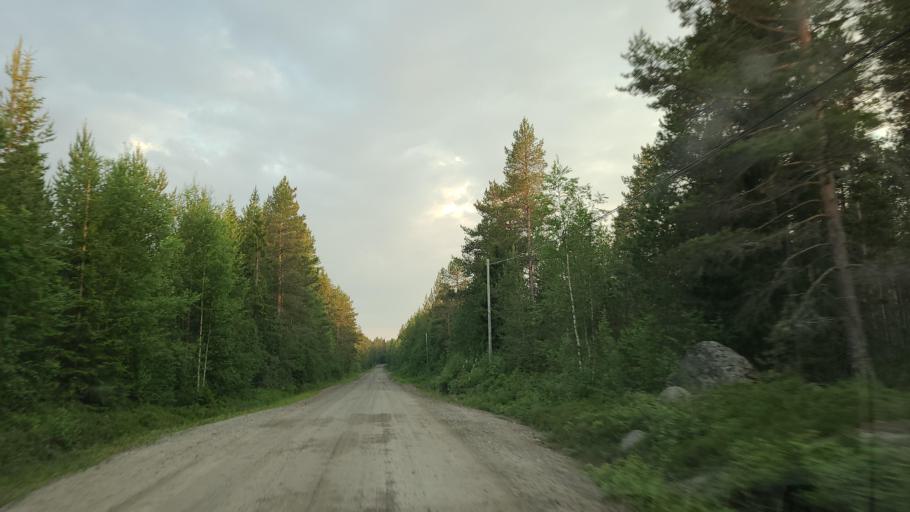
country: SE
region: Vaesterbotten
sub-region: Robertsfors Kommun
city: Robertsfors
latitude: 64.0750
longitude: 20.8846
